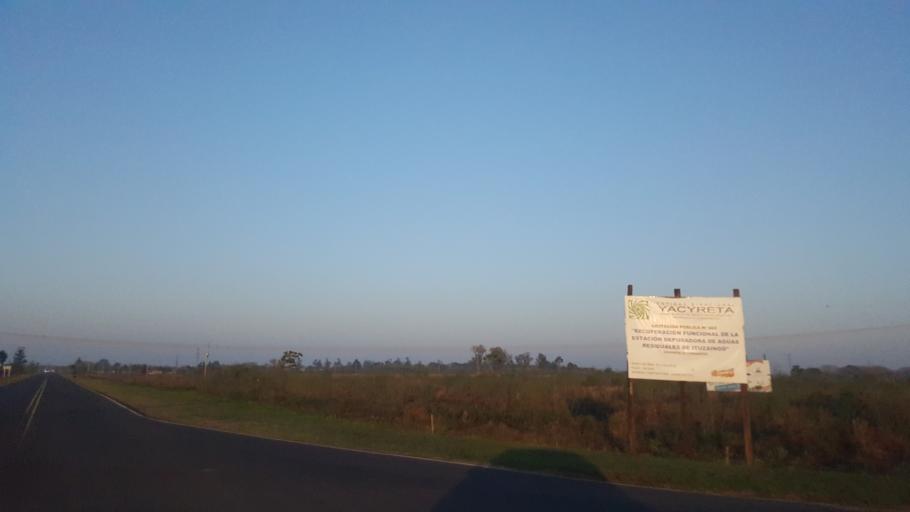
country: AR
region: Corrientes
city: Ituzaingo
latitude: -27.5601
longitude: -56.6557
